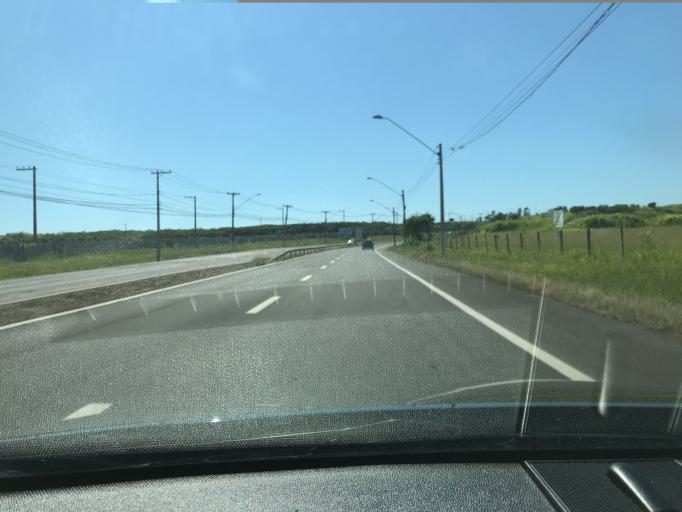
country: BR
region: Sao Paulo
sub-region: Campinas
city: Campinas
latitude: -22.8693
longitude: -47.0942
